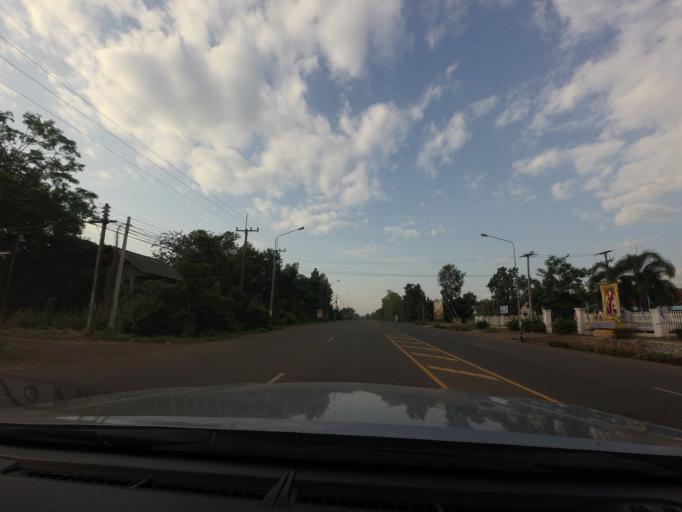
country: TH
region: Phitsanulok
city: Noen Maprang
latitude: 16.5820
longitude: 100.6297
